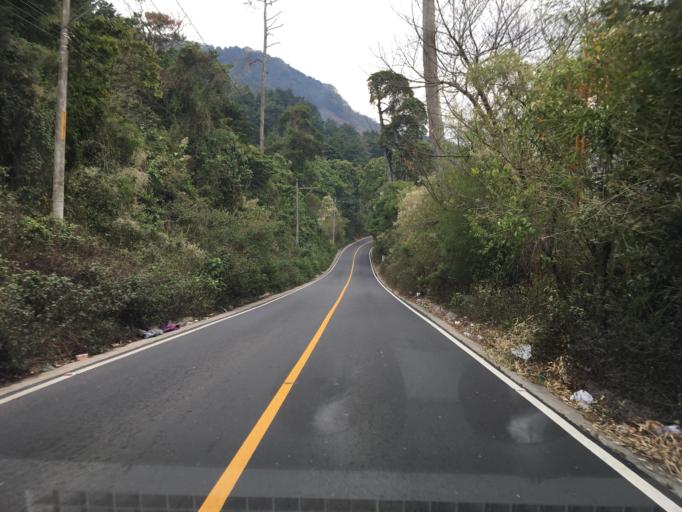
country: GT
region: Guatemala
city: Villa Canales
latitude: 14.4370
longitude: -90.5060
